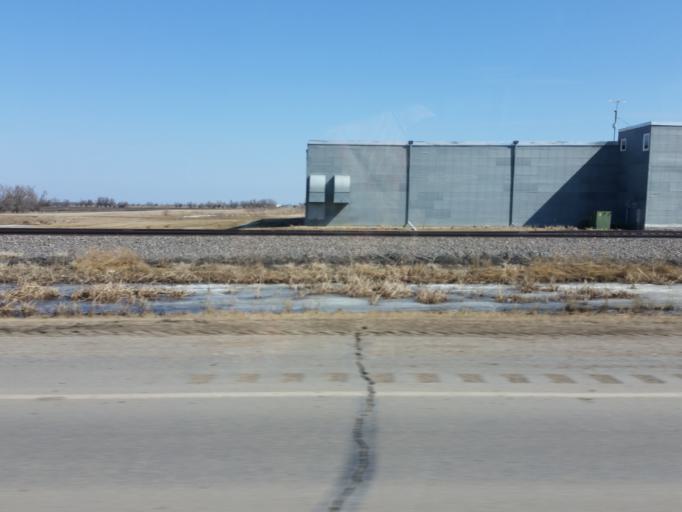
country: US
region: North Dakota
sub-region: Walsh County
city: Grafton
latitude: 48.2667
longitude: -97.3652
